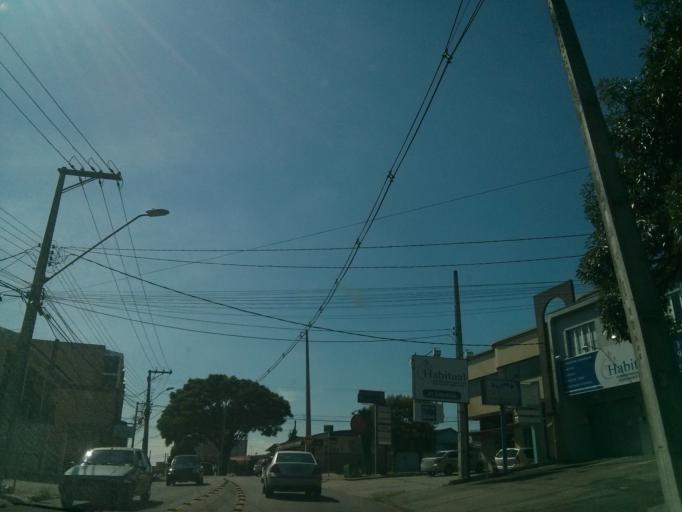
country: BR
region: Parana
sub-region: Sao Jose Dos Pinhais
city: Sao Jose dos Pinhais
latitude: -25.5506
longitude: -49.1955
